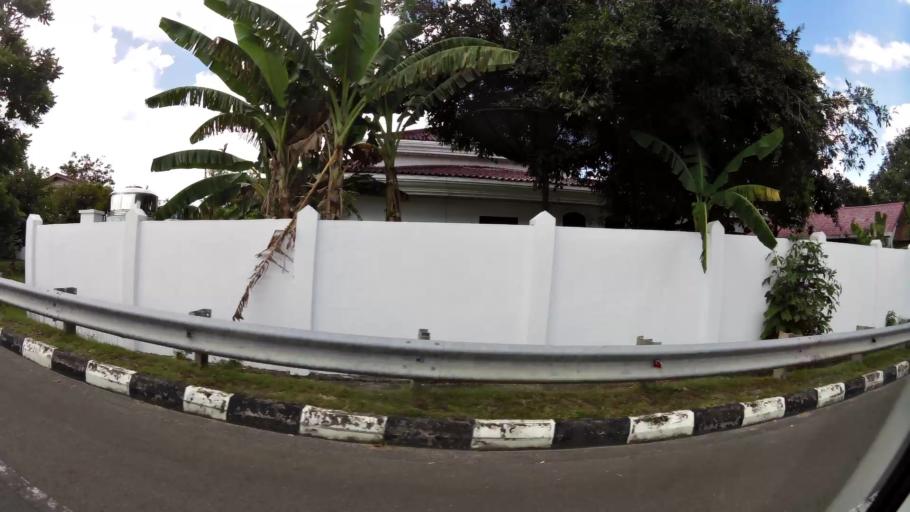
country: BN
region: Brunei and Muara
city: Bandar Seri Begawan
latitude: 4.9488
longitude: 114.9648
